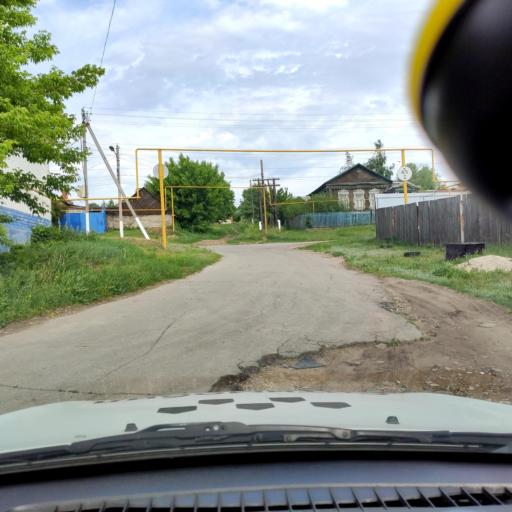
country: RU
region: Samara
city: Zhigulevsk
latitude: 53.5476
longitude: 49.5298
